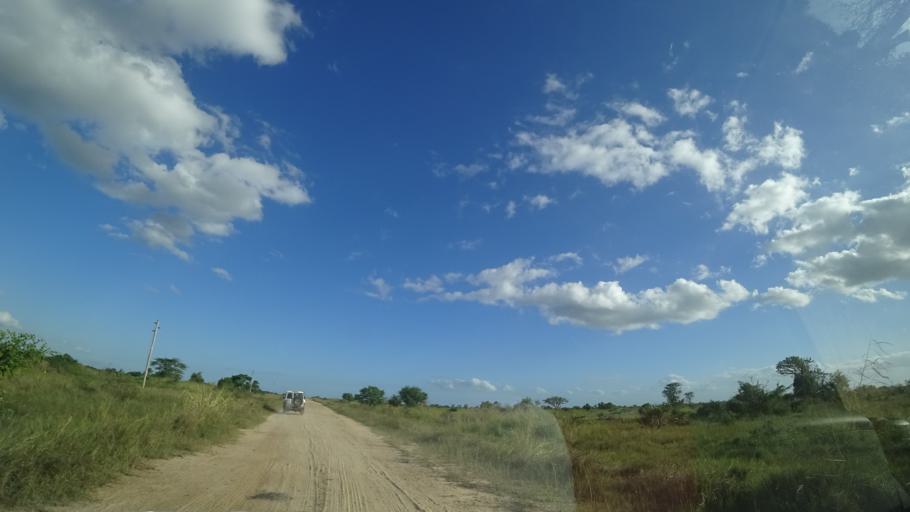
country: MZ
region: Sofala
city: Dondo
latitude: -19.4341
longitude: 34.5611
